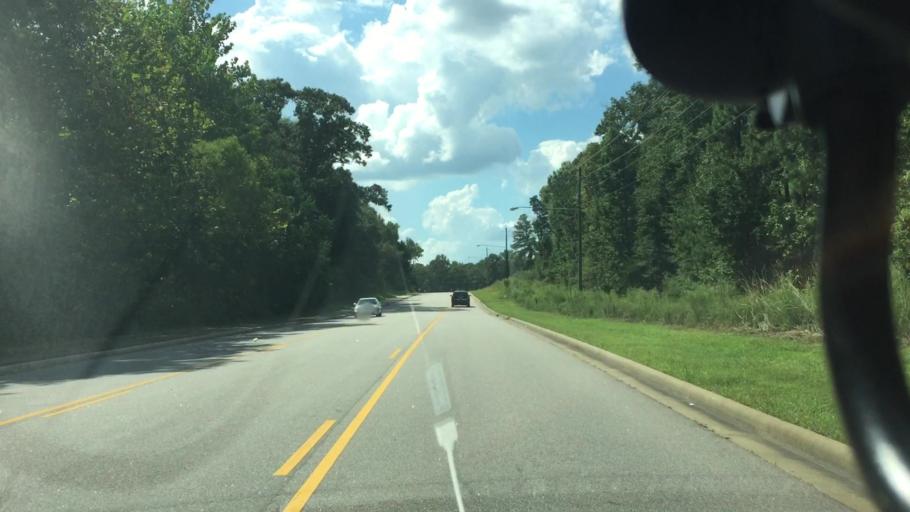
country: US
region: Alabama
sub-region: Lee County
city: Auburn
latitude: 32.5684
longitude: -85.5201
